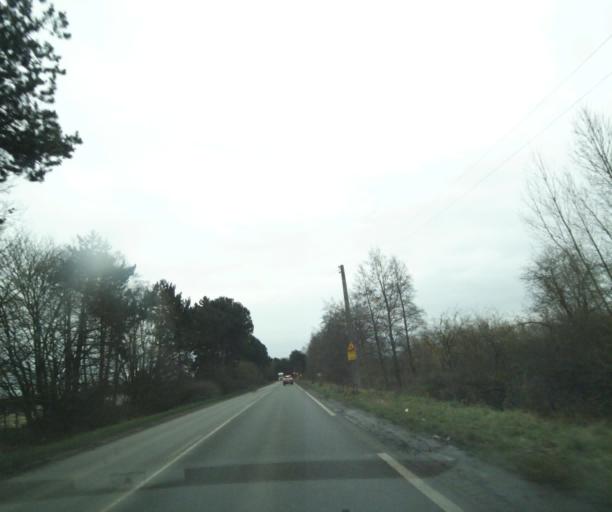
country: FR
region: Nord-Pas-de-Calais
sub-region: Departement du Nord
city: Vicq
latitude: 50.4060
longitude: 3.5923
